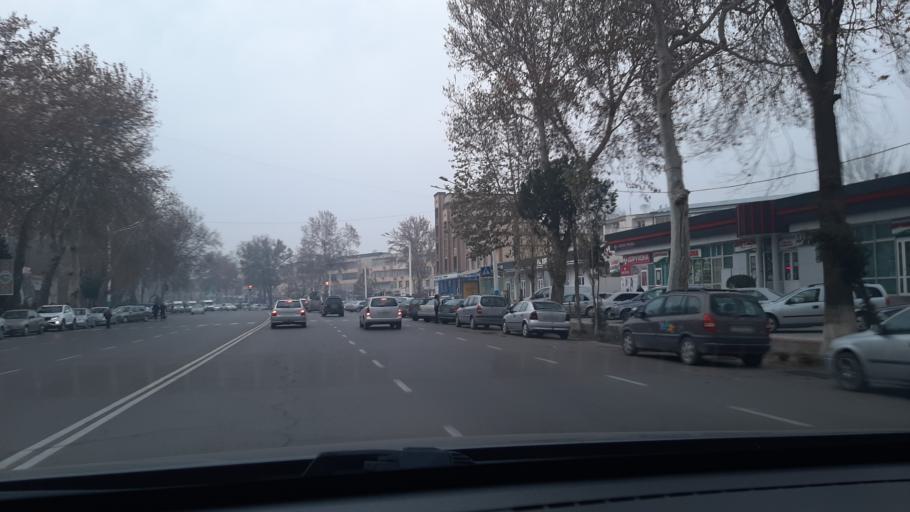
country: TJ
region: Viloyati Sughd
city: Khujand
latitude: 40.2749
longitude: 69.6374
